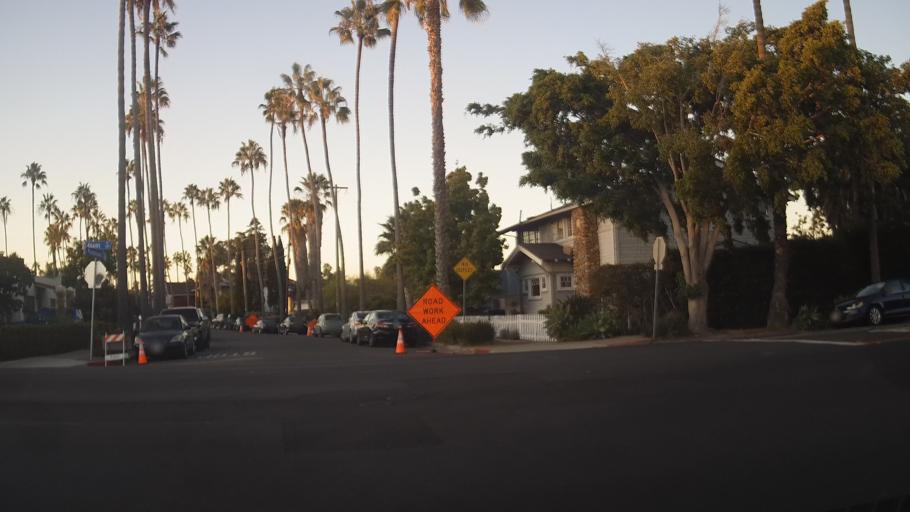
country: US
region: California
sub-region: San Diego County
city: San Diego
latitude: 32.7624
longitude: -117.1401
